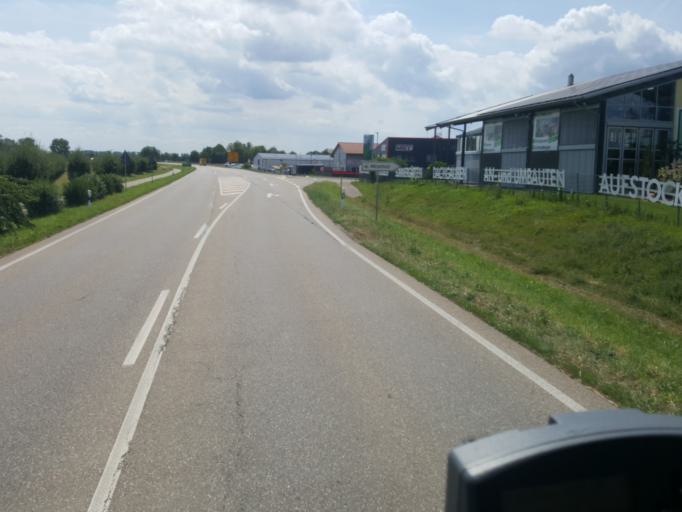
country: DE
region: Baden-Wuerttemberg
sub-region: Freiburg Region
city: Buggingen
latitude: 47.8512
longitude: 7.6290
